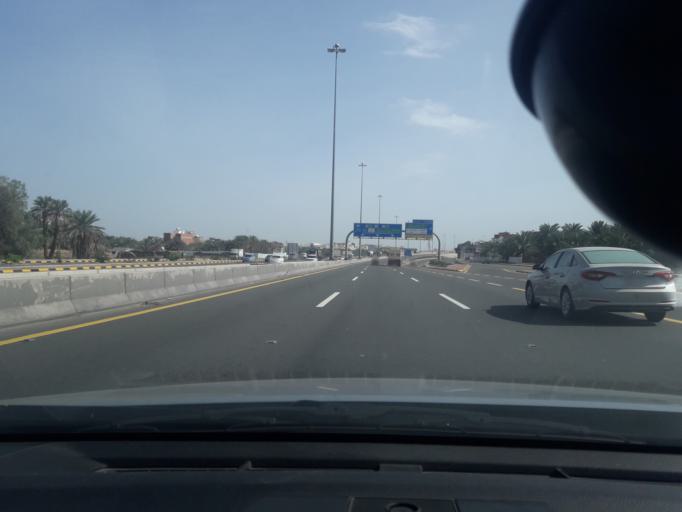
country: SA
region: Al Madinah al Munawwarah
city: Medina
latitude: 24.4422
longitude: 39.6330
